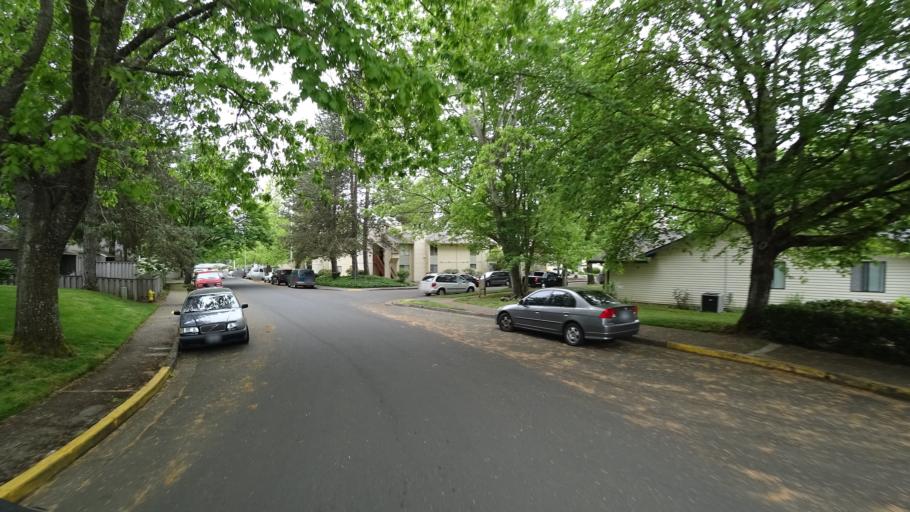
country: US
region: Oregon
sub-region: Washington County
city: Beaverton
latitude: 45.4716
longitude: -122.8027
